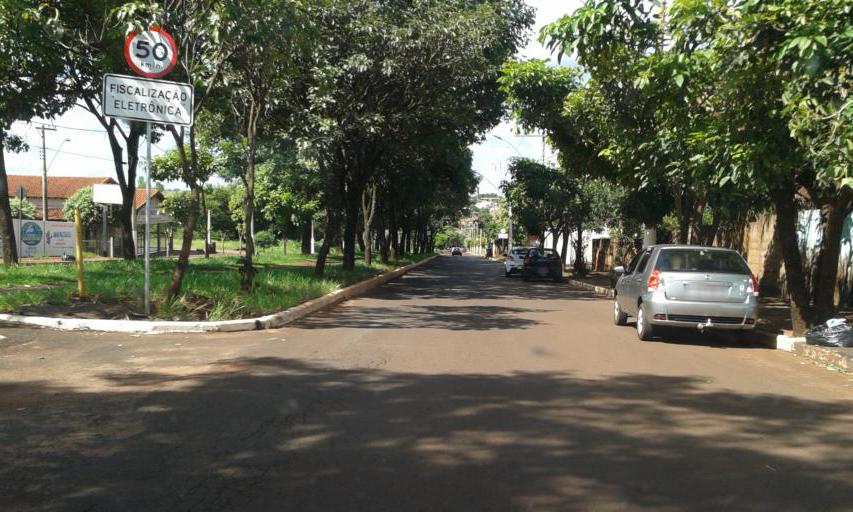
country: BR
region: Minas Gerais
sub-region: Ituiutaba
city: Ituiutaba
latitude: -18.9688
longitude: -49.4751
